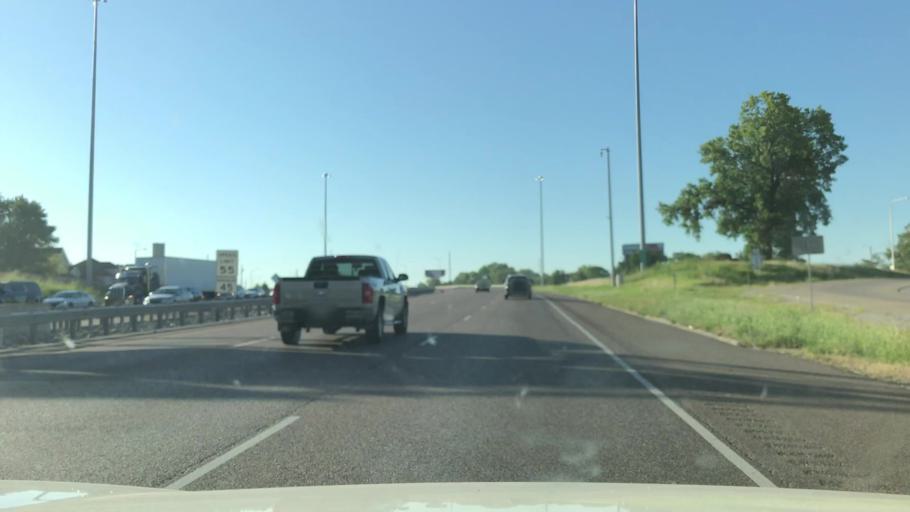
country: US
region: Illinois
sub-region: Saint Clair County
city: East Saint Louis
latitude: 38.6271
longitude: -90.1381
